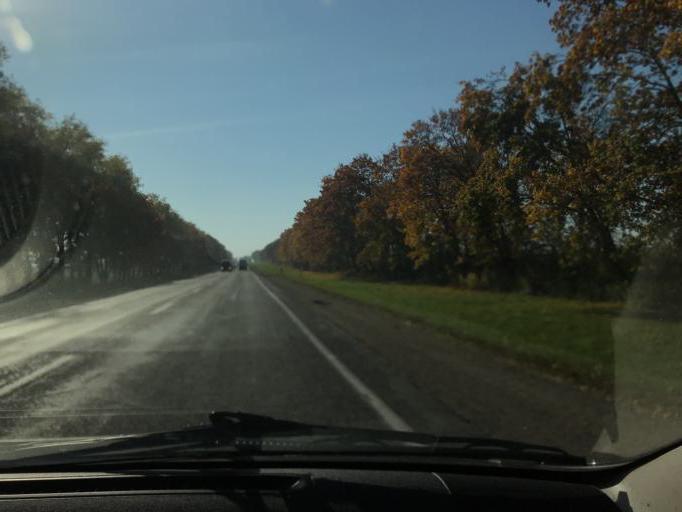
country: BY
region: Minsk
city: Salihorsk
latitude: 52.8866
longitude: 27.4706
